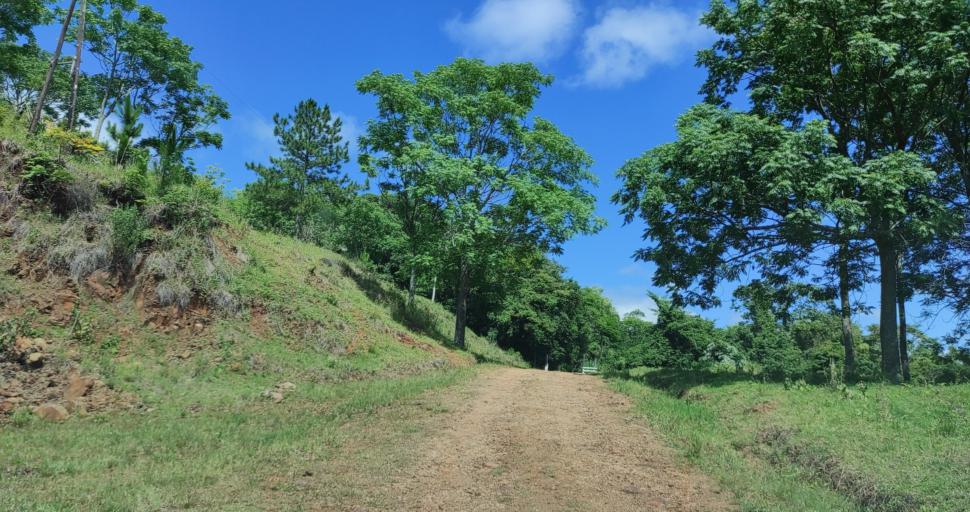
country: AR
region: Misiones
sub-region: Departamento de Veinticinco de Mayo
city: Veinticinco de Mayo
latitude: -27.4162
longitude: -54.7203
